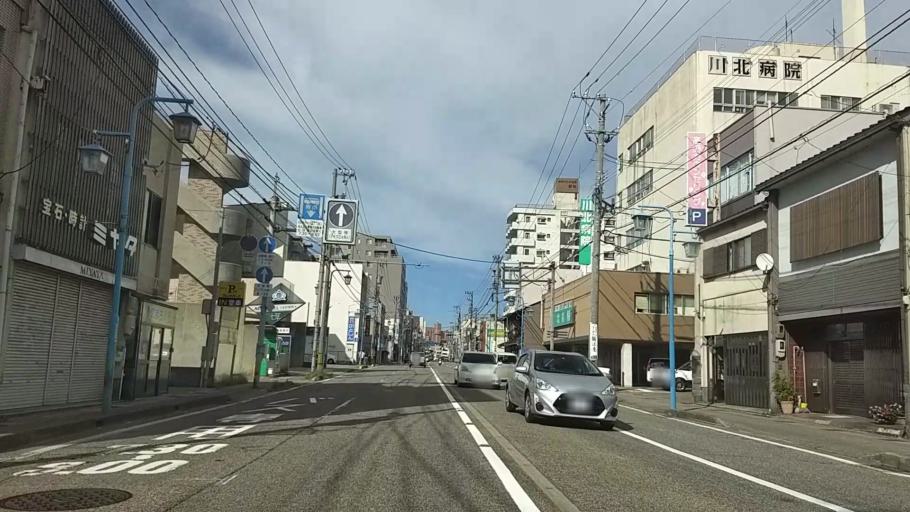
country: JP
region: Ishikawa
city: Nonoichi
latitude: 36.5538
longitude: 136.6467
